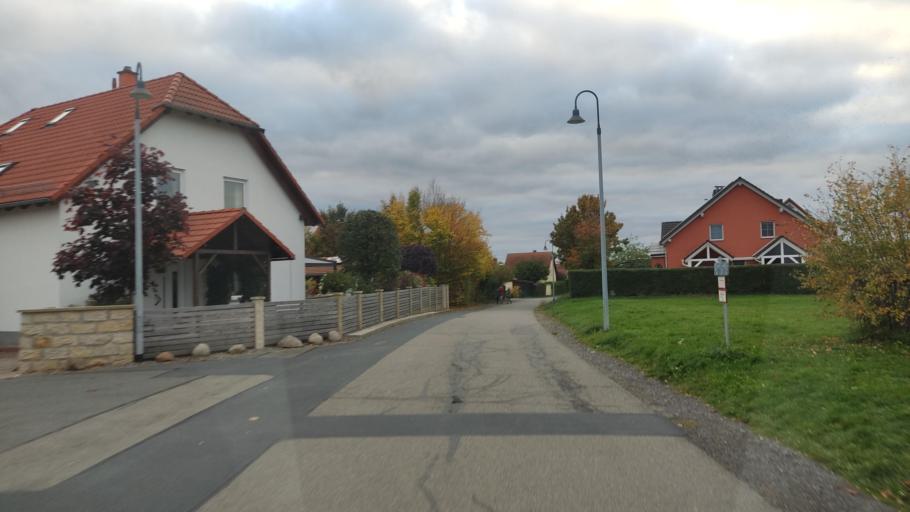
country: DE
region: Saxony
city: Tharandt
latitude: 51.0292
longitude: 13.5865
